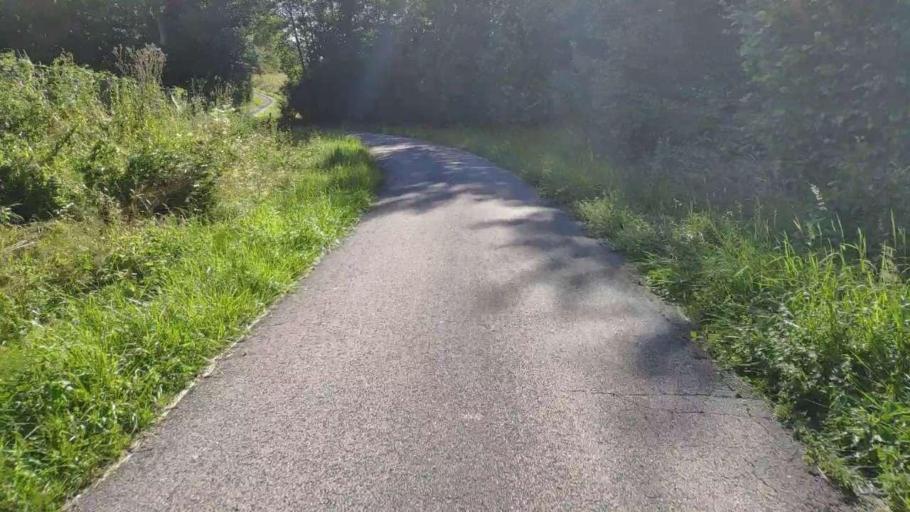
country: FR
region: Franche-Comte
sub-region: Departement du Jura
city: Bletterans
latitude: 46.8244
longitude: 5.5081
